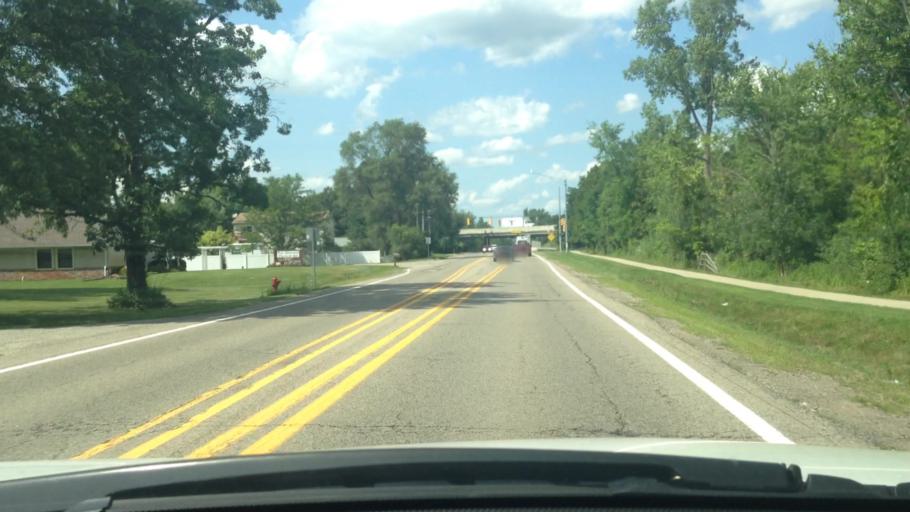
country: US
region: Michigan
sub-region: Oakland County
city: Waterford
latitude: 42.7184
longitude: -83.3492
